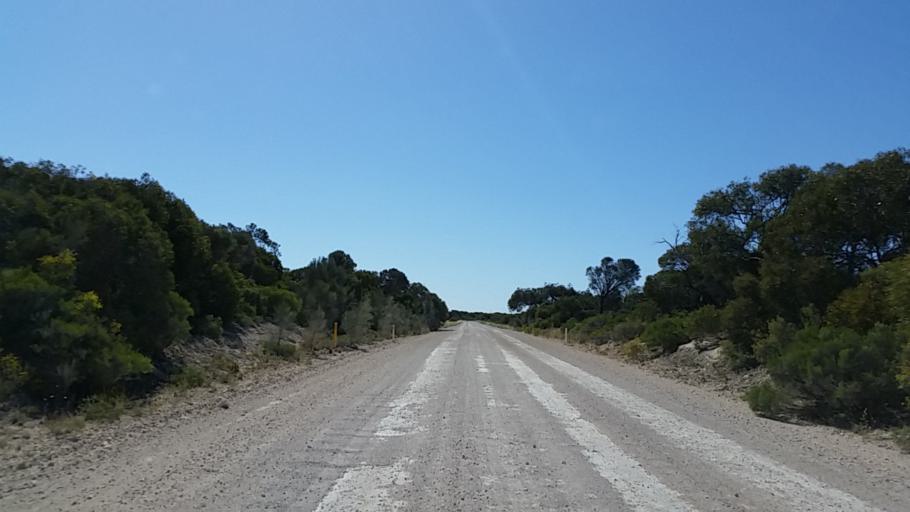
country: AU
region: South Australia
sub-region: Yorke Peninsula
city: Honiton
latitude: -35.2155
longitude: 137.0438
